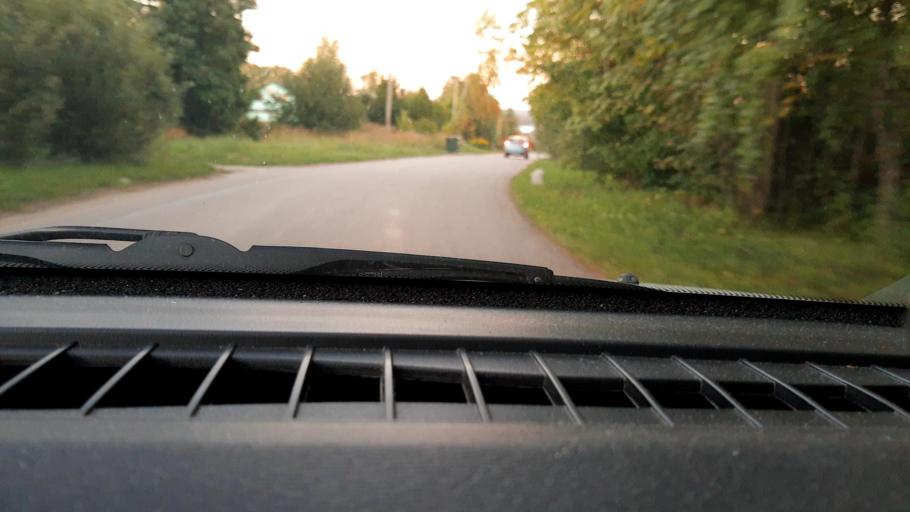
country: RU
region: Nizjnij Novgorod
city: Pamyat' Parizhskoy Kommuny
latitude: 56.0717
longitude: 44.4684
